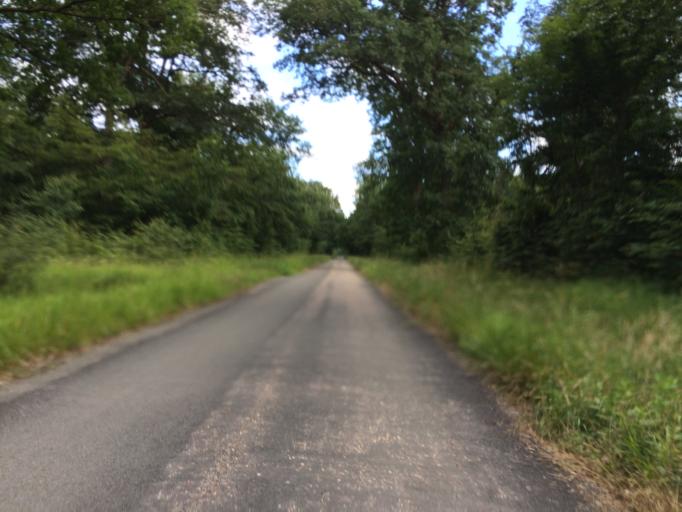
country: FR
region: Ile-de-France
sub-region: Departement de l'Essonne
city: Etiolles
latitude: 48.6609
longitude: 2.4839
